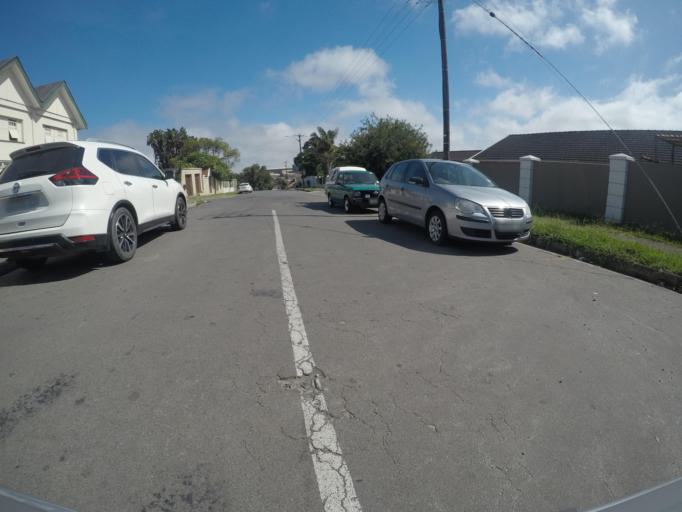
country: ZA
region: Eastern Cape
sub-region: Buffalo City Metropolitan Municipality
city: East London
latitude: -32.9804
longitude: 27.8931
